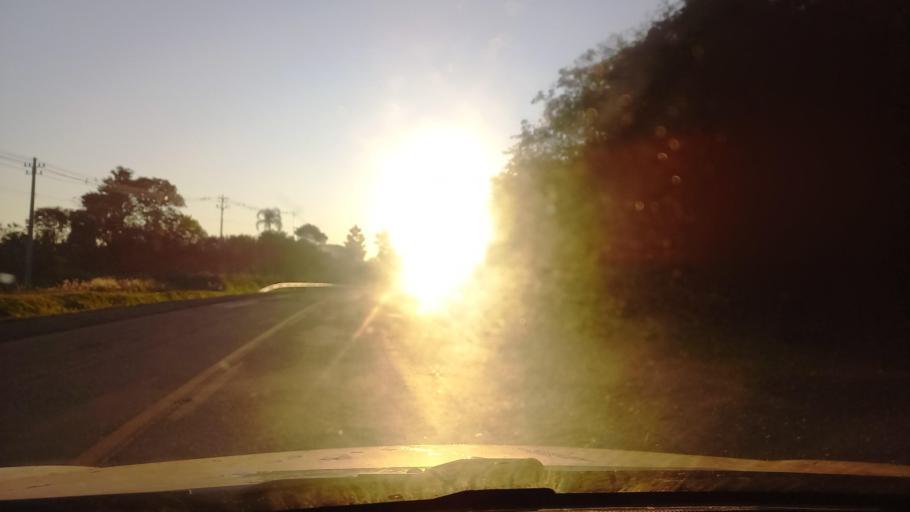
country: BR
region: Rio Grande do Sul
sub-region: Candelaria
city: Candelaria
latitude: -29.6817
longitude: -52.8421
